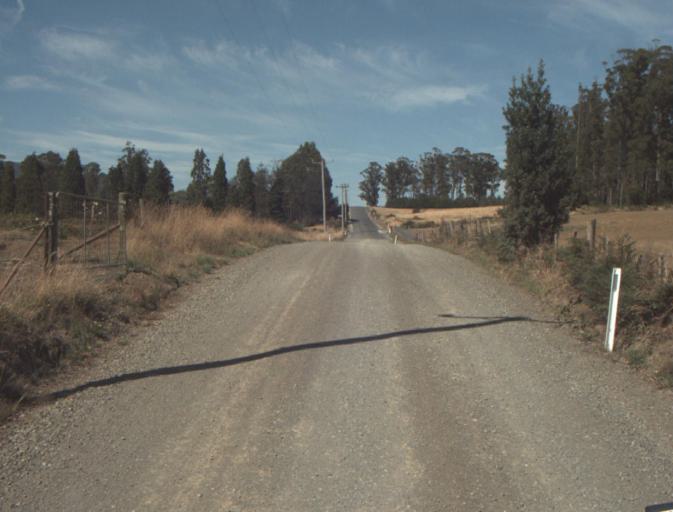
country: AU
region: Tasmania
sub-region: Launceston
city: Mayfield
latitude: -41.2290
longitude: 147.2359
